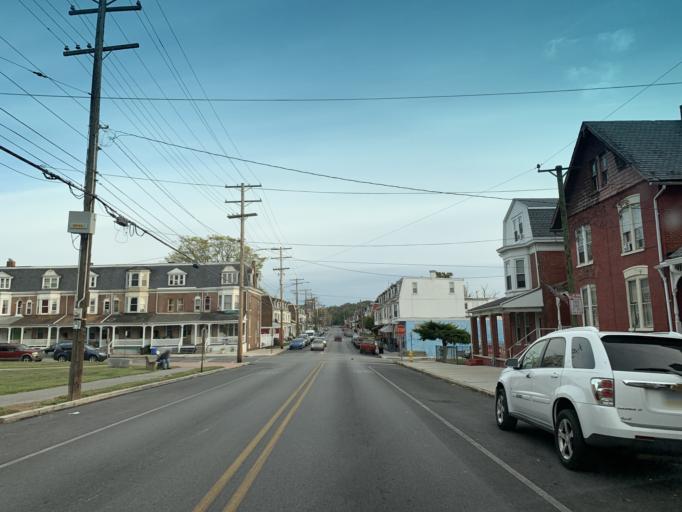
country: US
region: Pennsylvania
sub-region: York County
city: York
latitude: 39.9554
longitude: -76.7285
